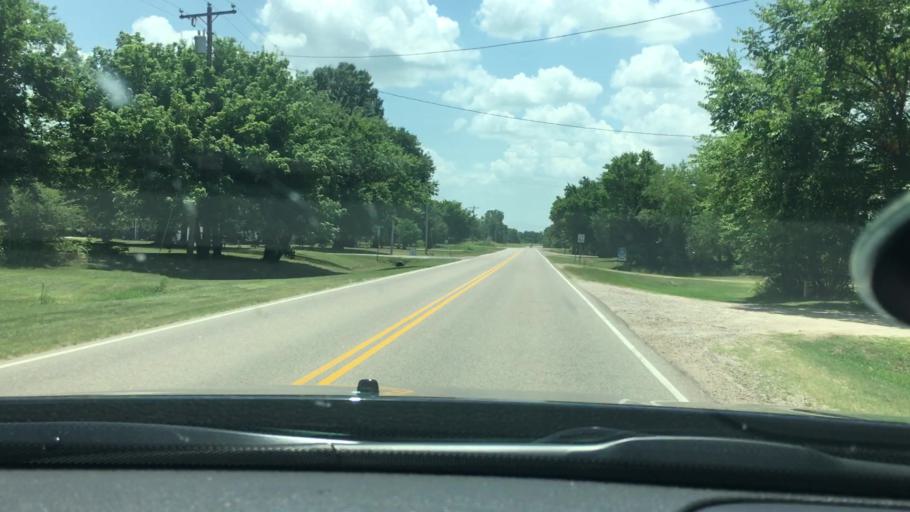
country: US
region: Oklahoma
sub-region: Johnston County
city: Tishomingo
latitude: 34.4914
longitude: -96.6273
